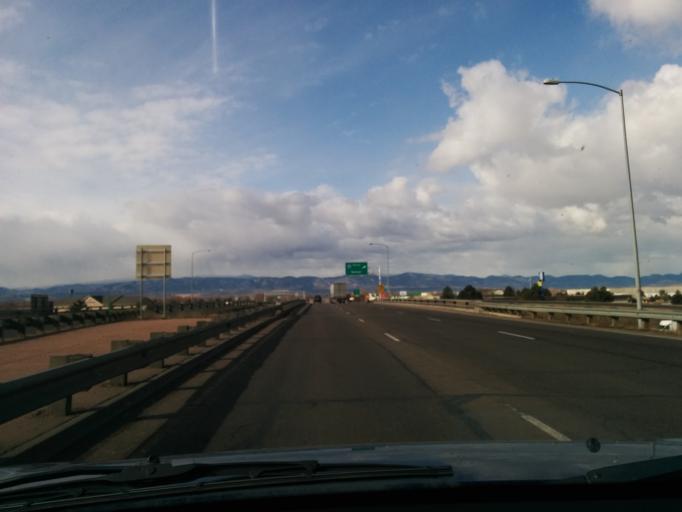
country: US
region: Colorado
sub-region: Larimer County
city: Fort Collins
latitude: 40.5812
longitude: -105.0005
